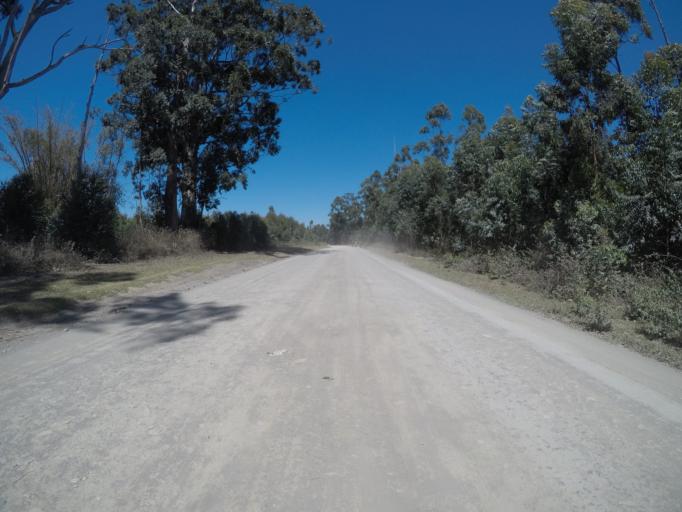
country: ZA
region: Eastern Cape
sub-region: OR Tambo District Municipality
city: Libode
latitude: -31.9567
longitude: 29.0233
